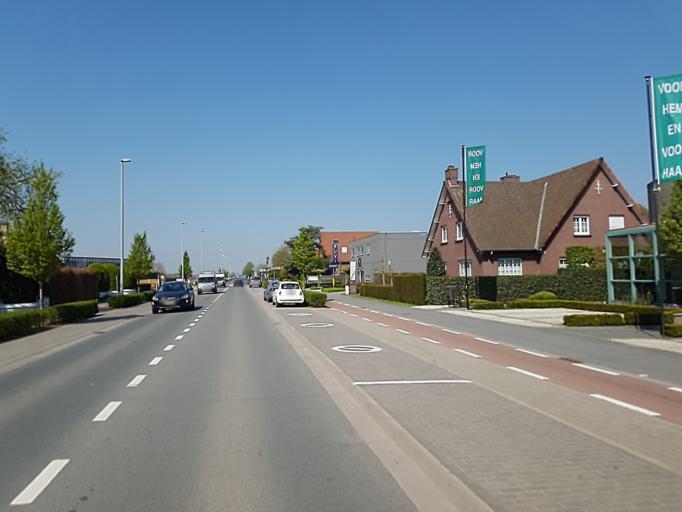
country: BE
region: Flanders
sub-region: Provincie West-Vlaanderen
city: Menen
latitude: 50.8036
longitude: 3.0981
